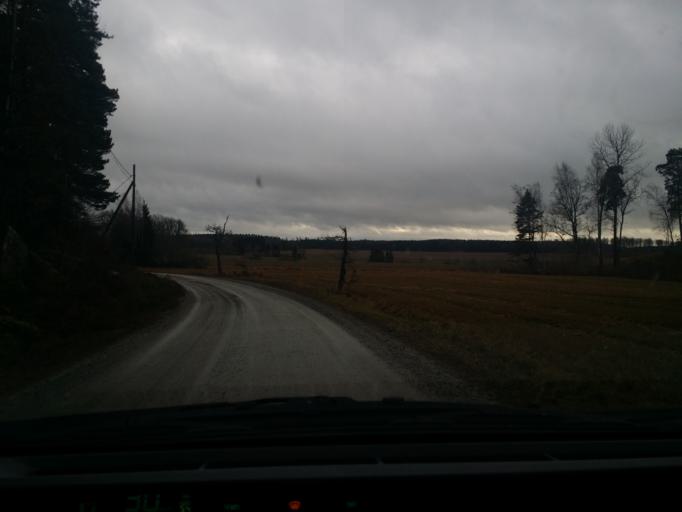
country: SE
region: Vaestmanland
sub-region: Vasteras
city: Skultuna
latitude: 59.7811
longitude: 16.3895
